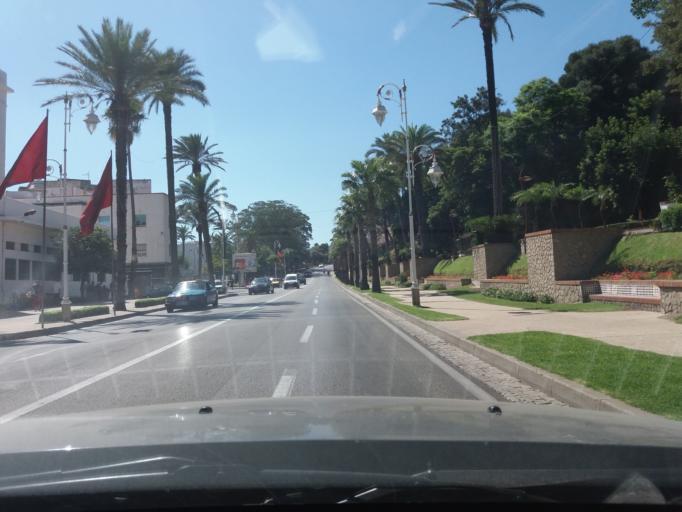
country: MA
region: Tanger-Tetouan
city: Tetouan
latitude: 35.5671
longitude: -5.3689
